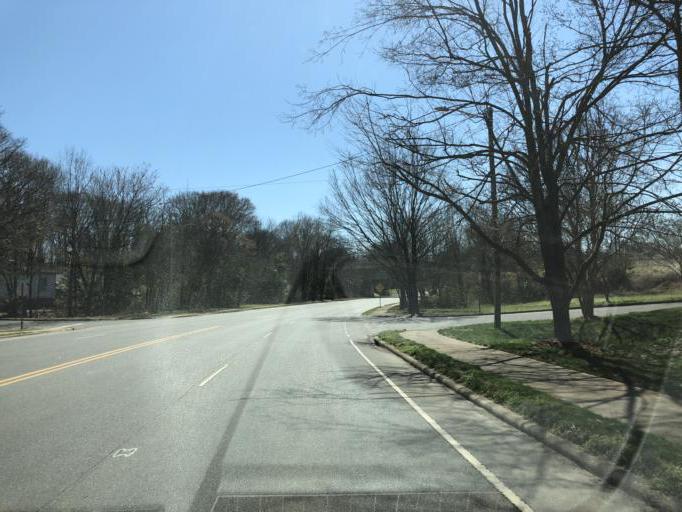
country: US
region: North Carolina
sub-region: Cleveland County
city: Shelby
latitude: 35.2995
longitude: -81.5353
